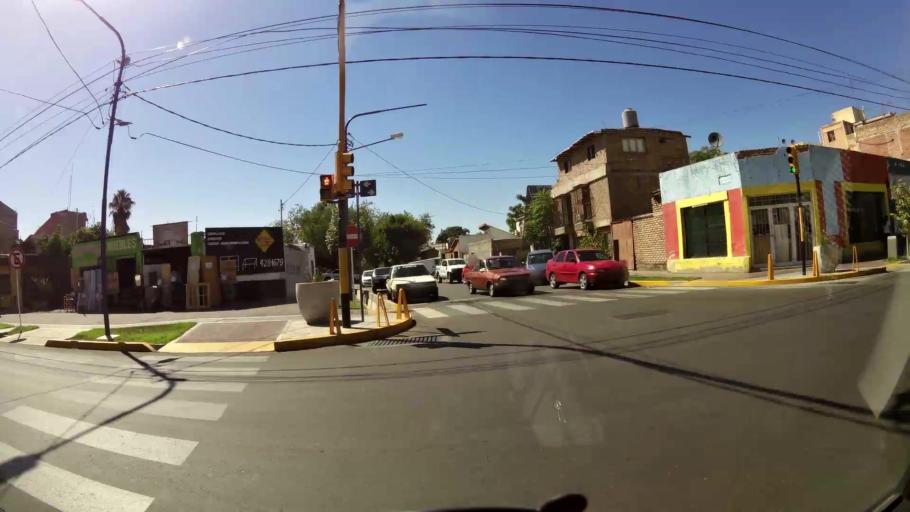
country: AR
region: Mendoza
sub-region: Departamento de Godoy Cruz
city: Godoy Cruz
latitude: -32.9077
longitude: -68.8607
